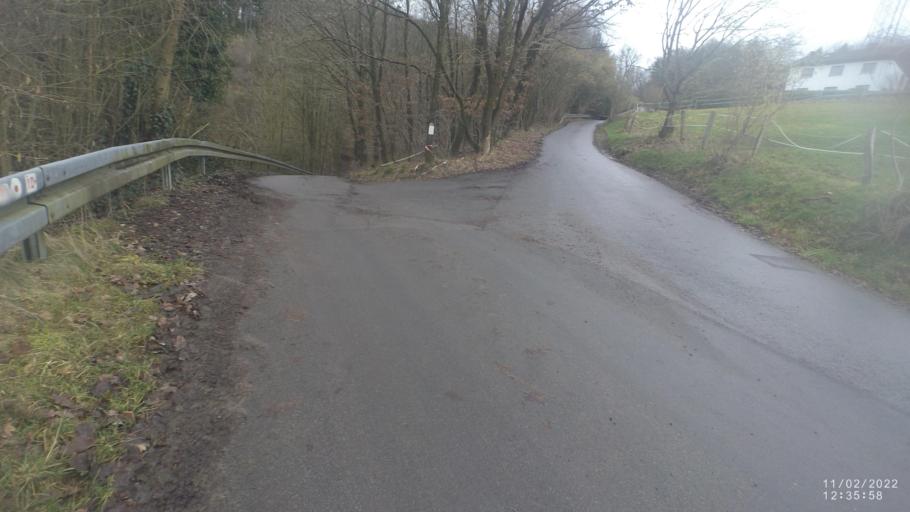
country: DE
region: North Rhine-Westphalia
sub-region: Regierungsbezirk Arnsberg
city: Nachrodt-Wiblingwerde
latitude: 51.3128
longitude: 7.6273
